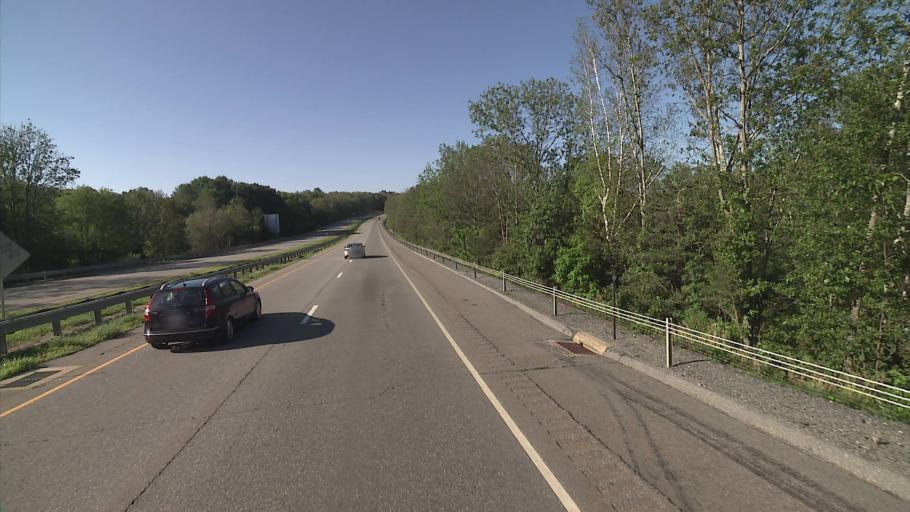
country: US
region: Connecticut
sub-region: Windham County
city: Wauregan
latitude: 41.7444
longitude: -71.8796
